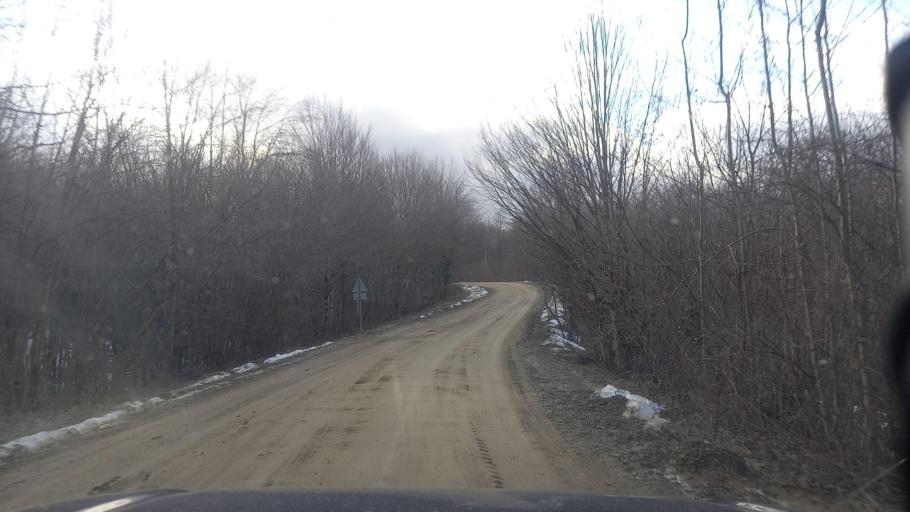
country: RU
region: Krasnodarskiy
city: Smolenskaya
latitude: 44.5848
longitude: 38.8107
